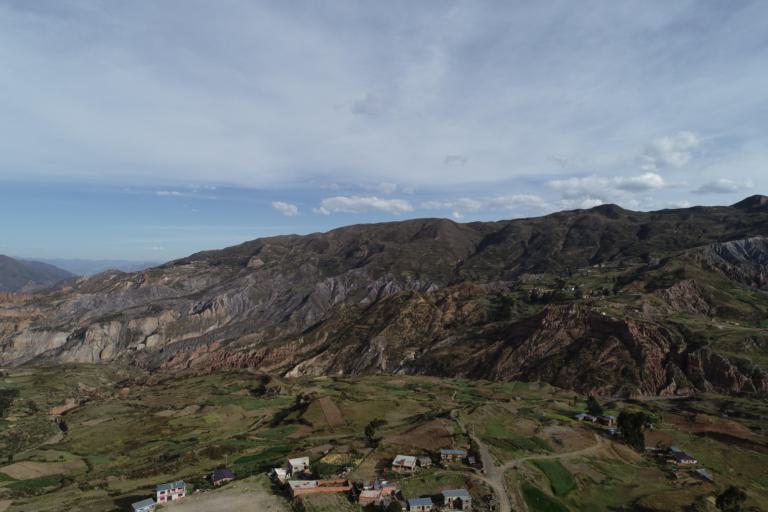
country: BO
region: La Paz
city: La Paz
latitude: -16.5447
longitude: -68.0000
